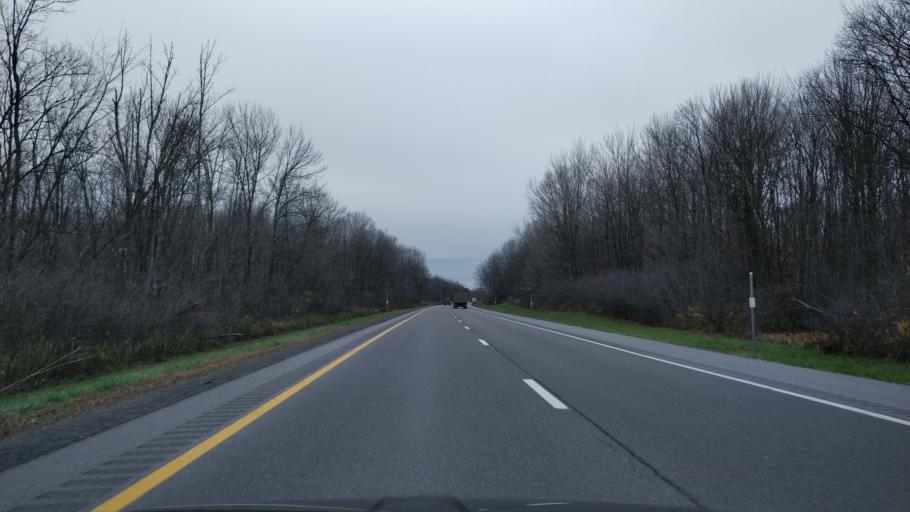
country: US
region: New York
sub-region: Oswego County
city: Pulaski
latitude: 43.6173
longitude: -76.0871
